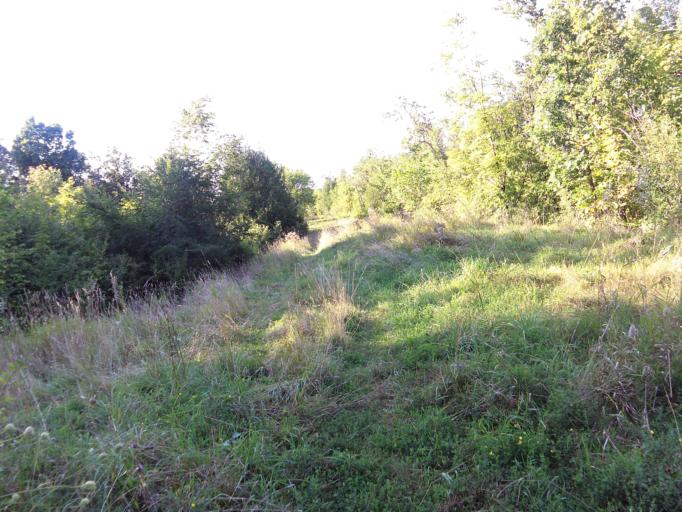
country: CA
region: Ontario
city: Ottawa
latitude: 45.4309
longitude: -75.7462
